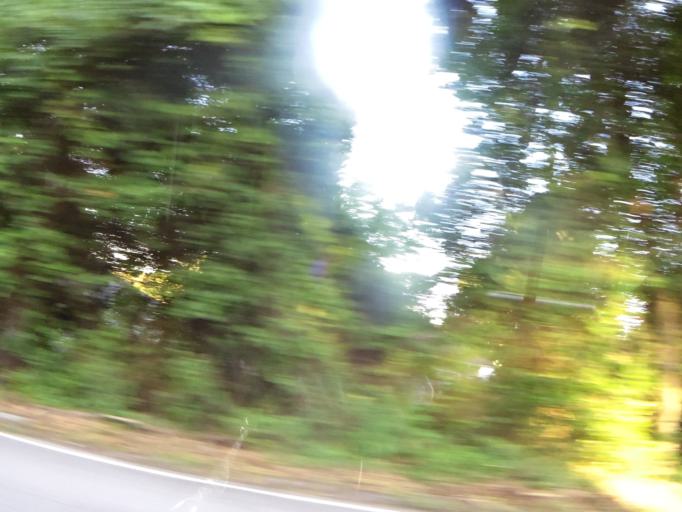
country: US
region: Florida
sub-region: Duval County
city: Atlantic Beach
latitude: 30.3825
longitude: -81.4971
